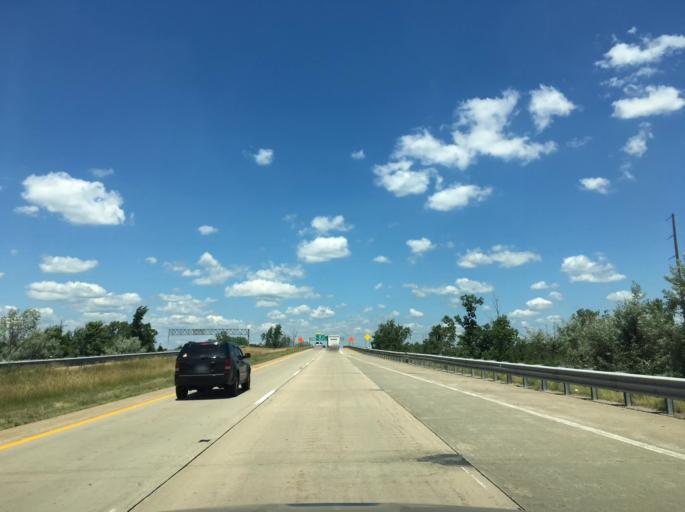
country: US
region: Michigan
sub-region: Midland County
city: Midland
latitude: 43.6060
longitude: -84.1617
